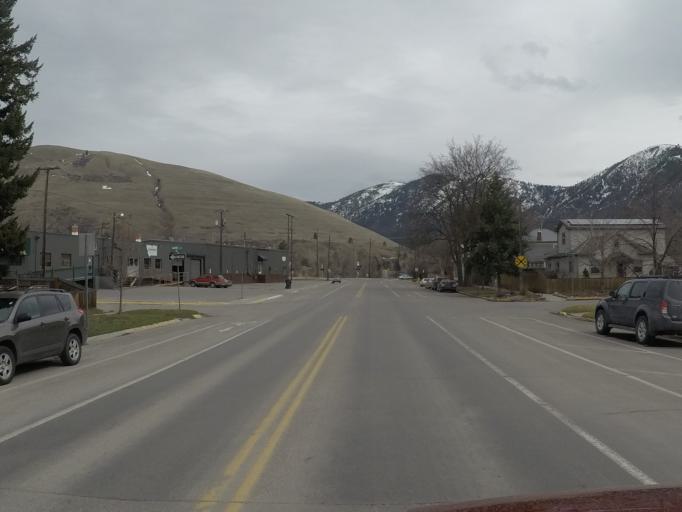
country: US
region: Montana
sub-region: Missoula County
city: Missoula
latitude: 46.8725
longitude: -113.9876
